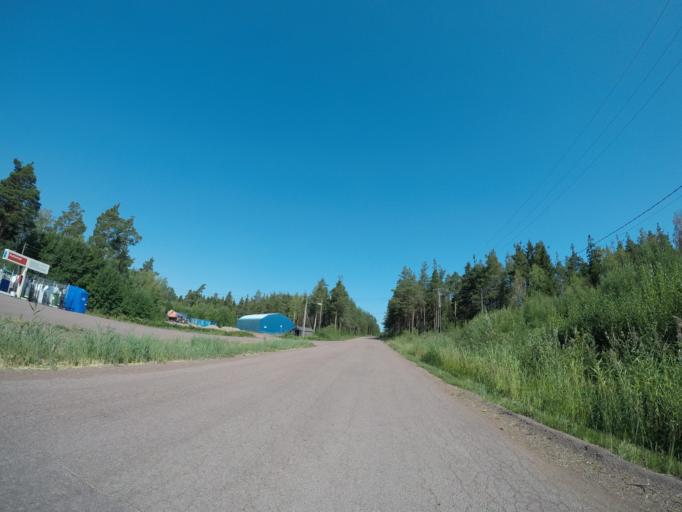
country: AX
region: Alands landsbygd
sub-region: Saltvik
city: Saltvik
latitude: 60.2283
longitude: 20.0089
